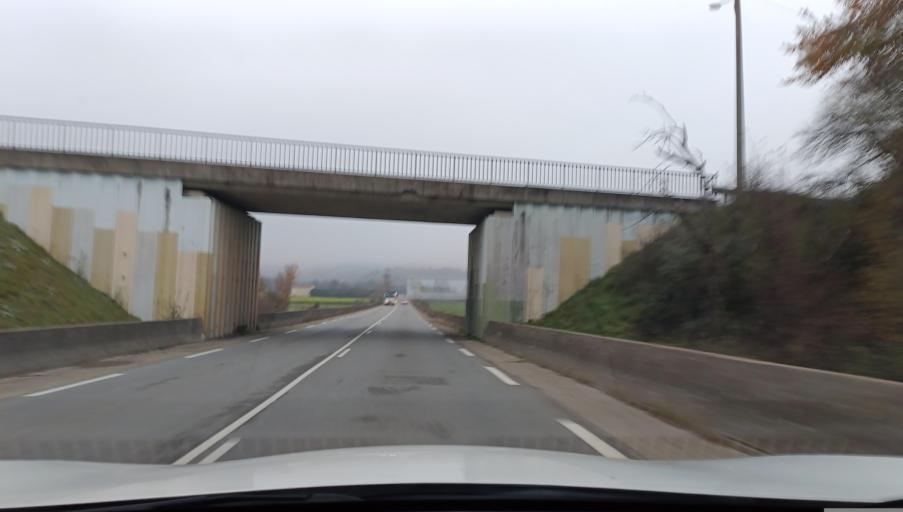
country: FR
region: Rhone-Alpes
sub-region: Departement de l'Isere
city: Pont-Eveque
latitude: 45.5330
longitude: 4.9292
